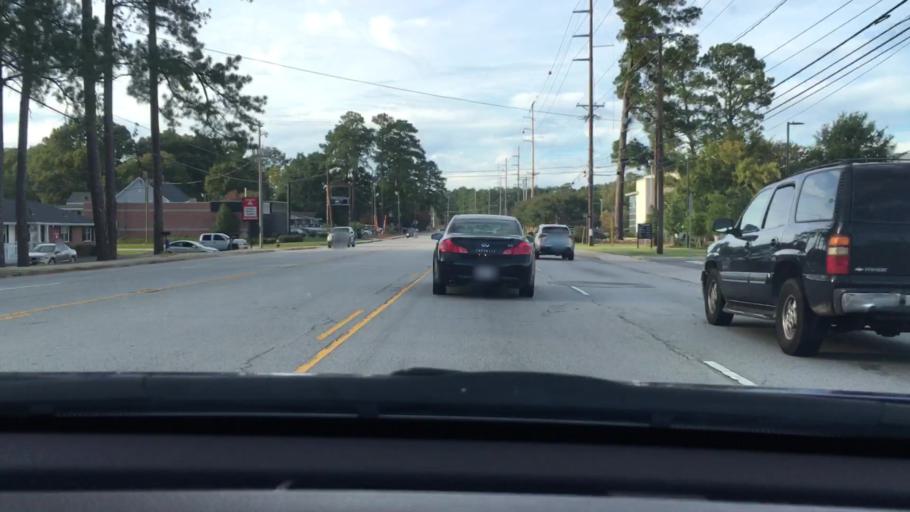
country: US
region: South Carolina
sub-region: Lexington County
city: Saint Andrews
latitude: 34.0662
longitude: -81.1168
